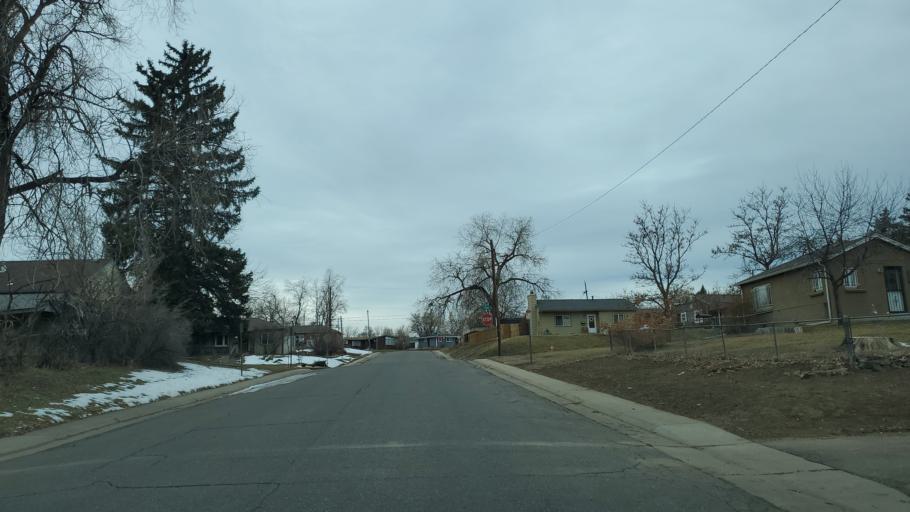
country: US
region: Colorado
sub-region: Denver County
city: Denver
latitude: 39.7018
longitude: -105.0047
